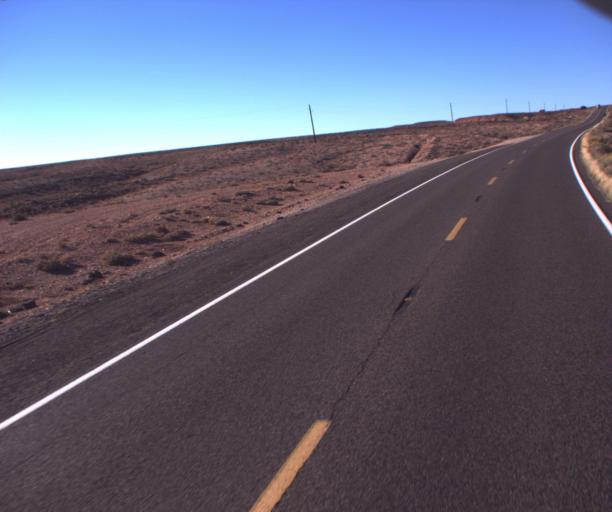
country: US
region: Arizona
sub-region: Coconino County
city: Page
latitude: 36.7597
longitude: -111.7126
